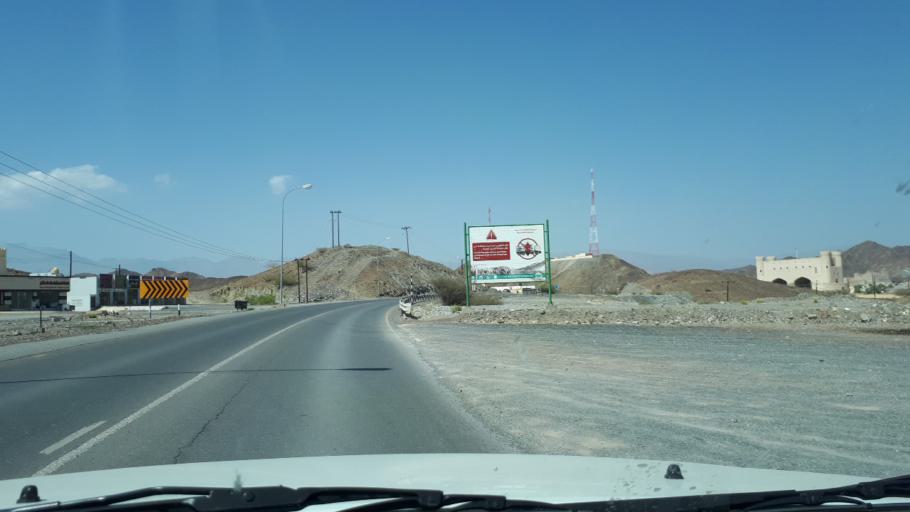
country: OM
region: Muhafazat ad Dakhiliyah
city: Bahla'
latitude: 22.9567
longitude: 57.2879
